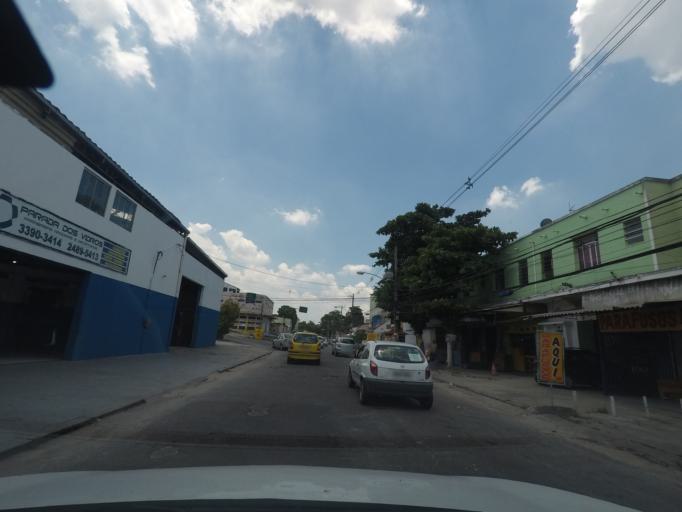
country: BR
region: Rio de Janeiro
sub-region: Sao Joao De Meriti
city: Sao Joao de Meriti
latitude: -22.8633
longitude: -43.3628
